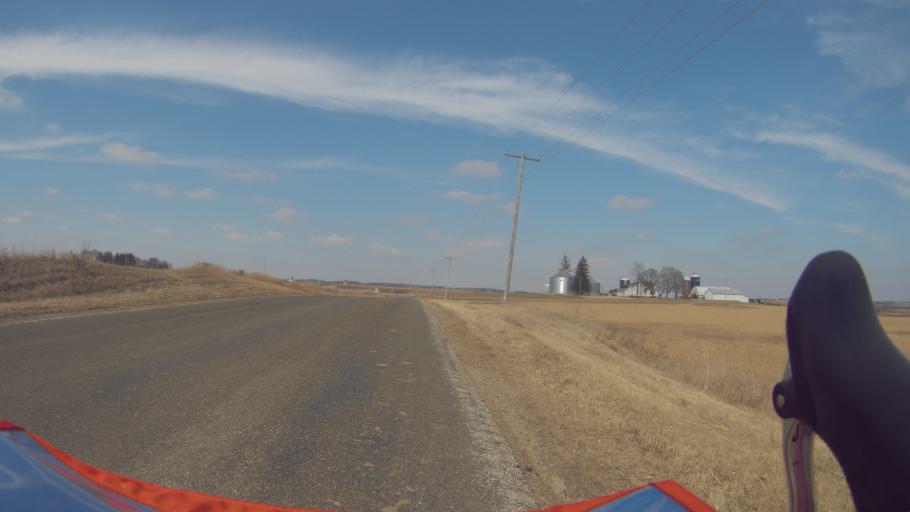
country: US
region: Wisconsin
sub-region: Dane County
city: Waunakee
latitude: 43.1610
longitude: -89.4921
